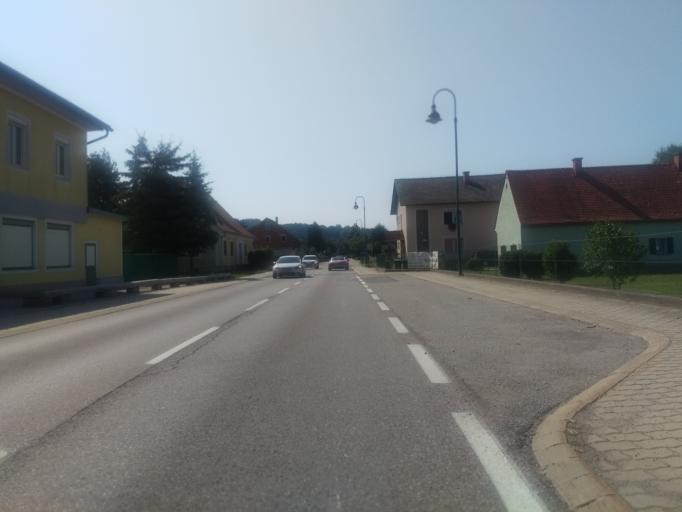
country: AT
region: Styria
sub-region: Politischer Bezirk Graz-Umgebung
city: Fernitz
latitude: 46.9694
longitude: 15.5012
